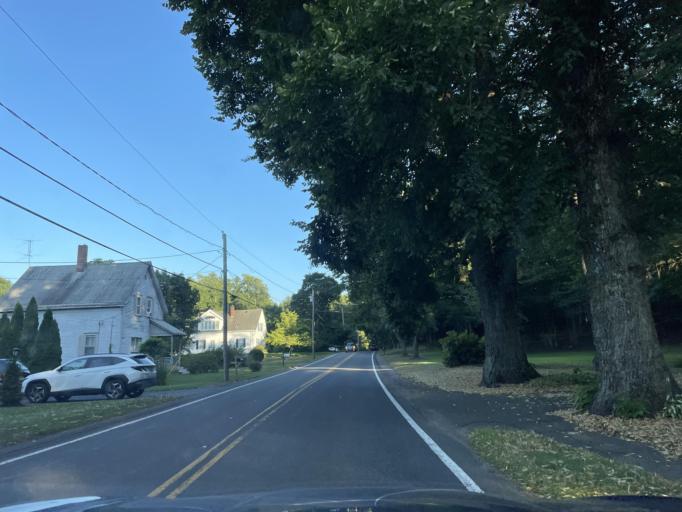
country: US
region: Massachusetts
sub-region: Plymouth County
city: East Bridgewater
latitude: 42.0110
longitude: -70.9593
